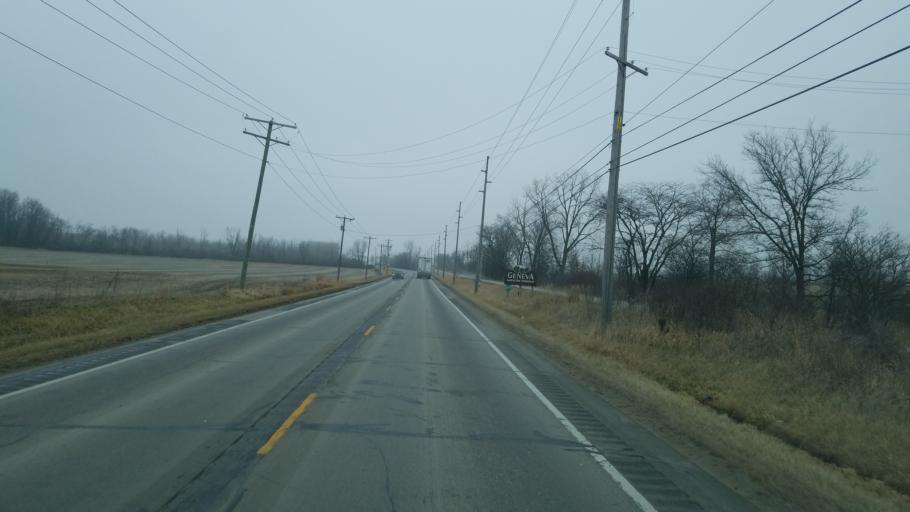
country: US
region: Indiana
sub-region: Adams County
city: Geneva
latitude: 40.5732
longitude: -84.9587
